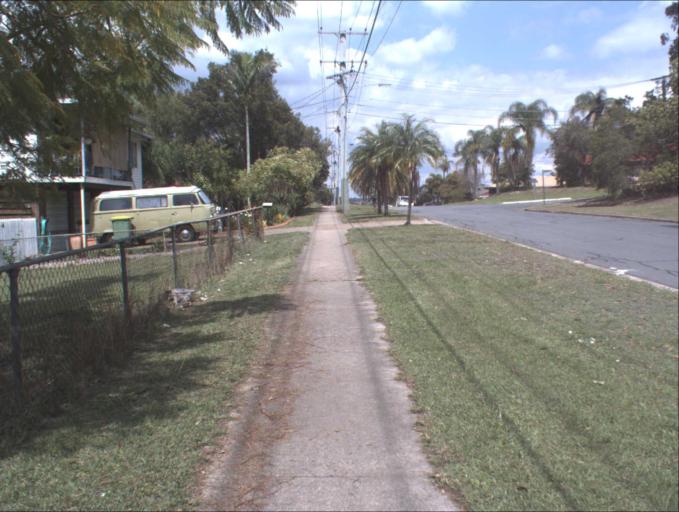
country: AU
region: Queensland
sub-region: Brisbane
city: Sunnybank Hills
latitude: -27.6589
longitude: 153.0500
